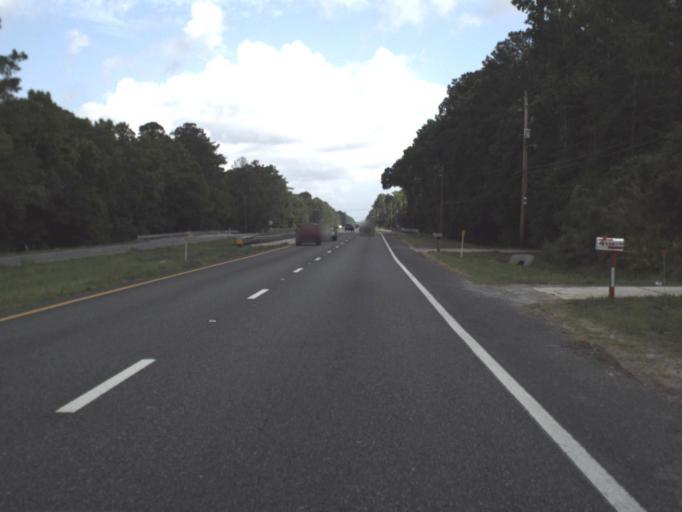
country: US
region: Florida
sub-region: Saint Johns County
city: Saint Augustine Shores
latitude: 29.7731
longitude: -81.3156
